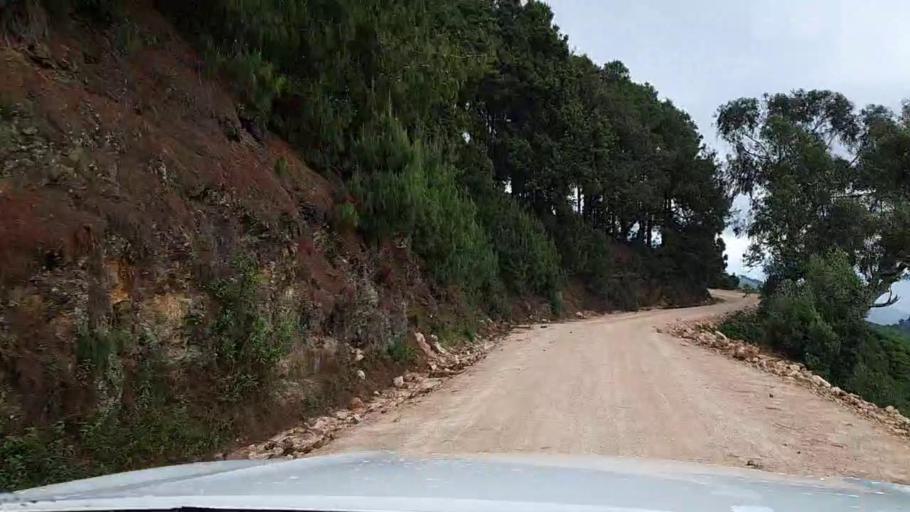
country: RW
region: Western Province
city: Kibuye
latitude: -2.3020
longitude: 29.3829
